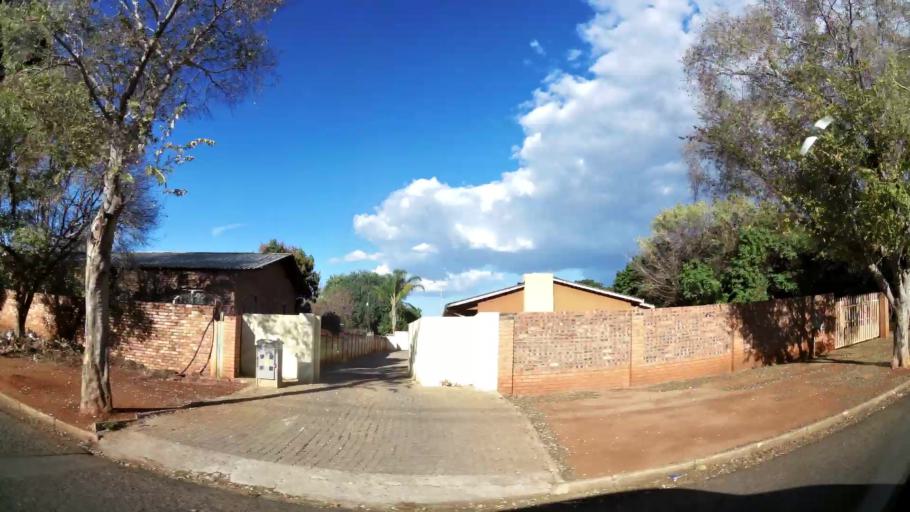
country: ZA
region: Limpopo
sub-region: Waterberg District Municipality
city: Mokopane
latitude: -24.1857
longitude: 28.9987
